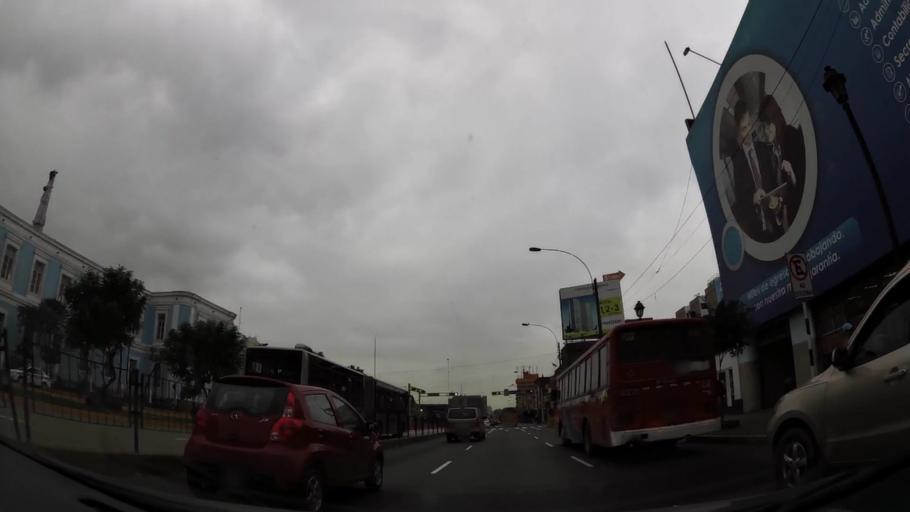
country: PE
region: Lima
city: Lima
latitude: -12.0556
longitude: -77.0422
